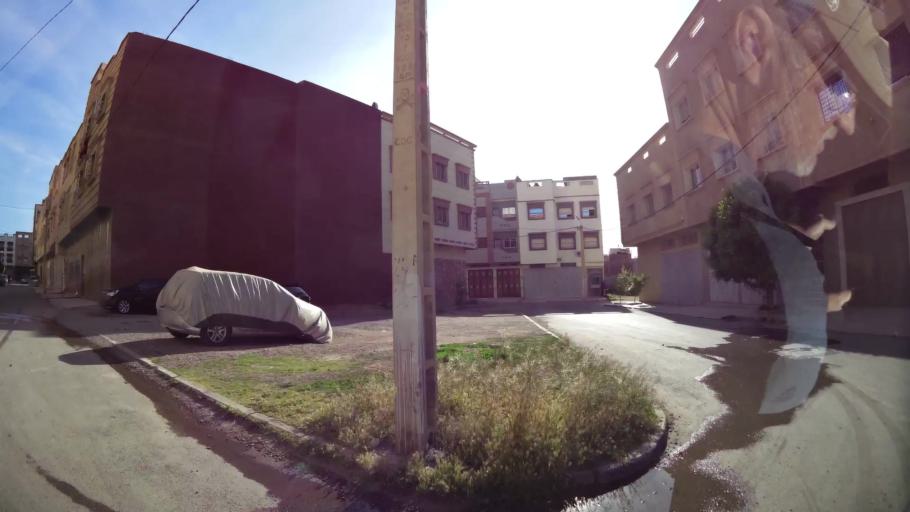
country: MA
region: Oriental
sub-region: Oujda-Angad
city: Oujda
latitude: 34.6711
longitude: -1.8946
